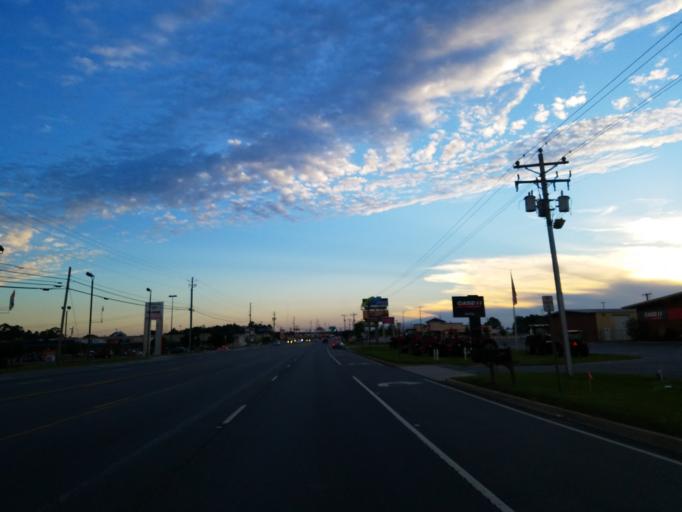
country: US
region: Georgia
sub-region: Tift County
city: Tifton
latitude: 31.4464
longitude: -83.5415
